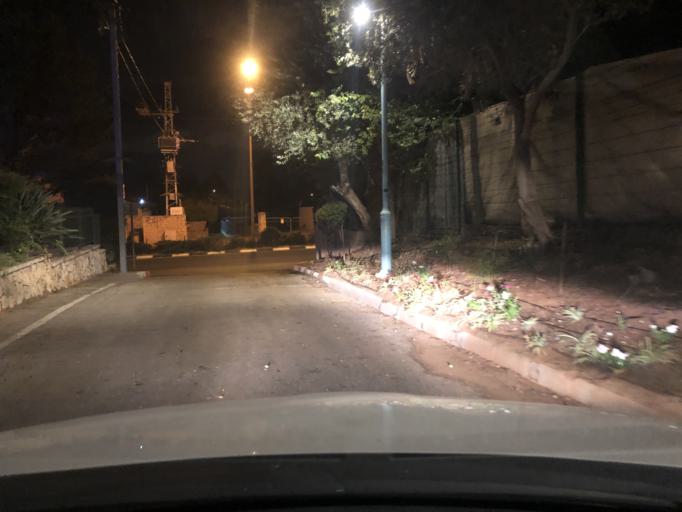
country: IL
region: Central District
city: Hod HaSharon
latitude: 32.1690
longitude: 34.8941
